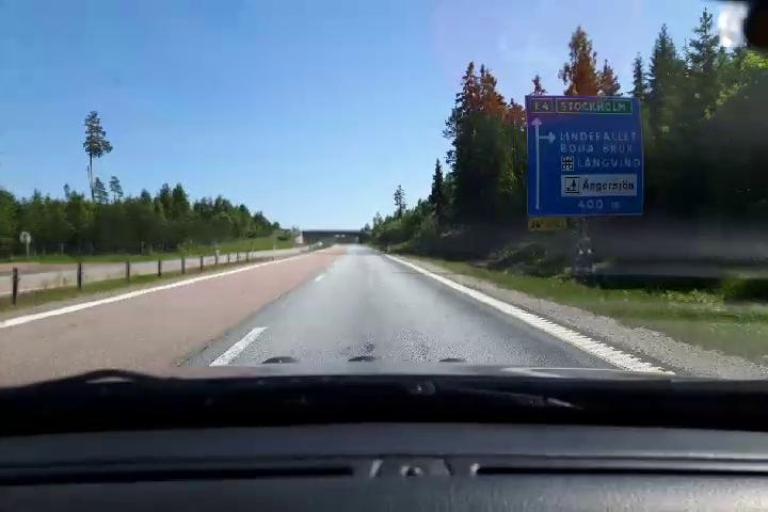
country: SE
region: Gaevleborg
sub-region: Hudiksvalls Kommun
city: Iggesund
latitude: 61.5236
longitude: 16.9746
